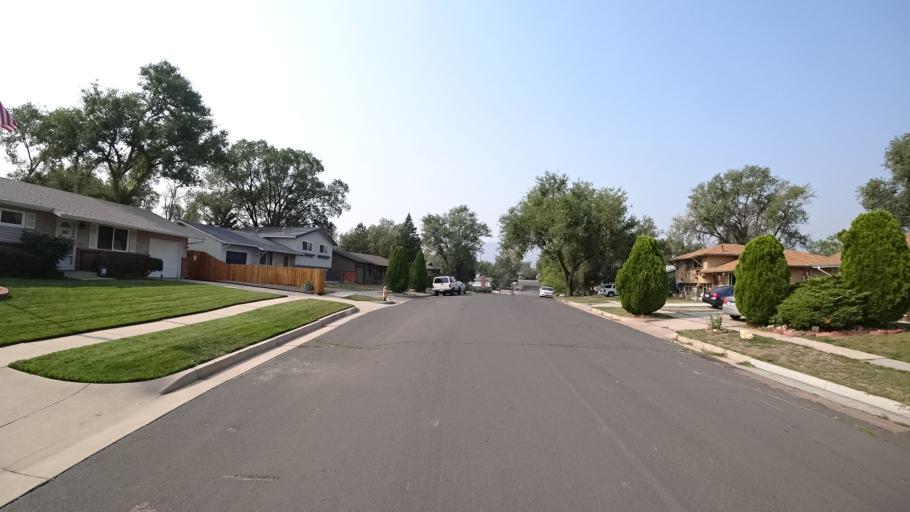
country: US
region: Colorado
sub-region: El Paso County
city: Stratmoor
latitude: 38.8142
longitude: -104.7773
